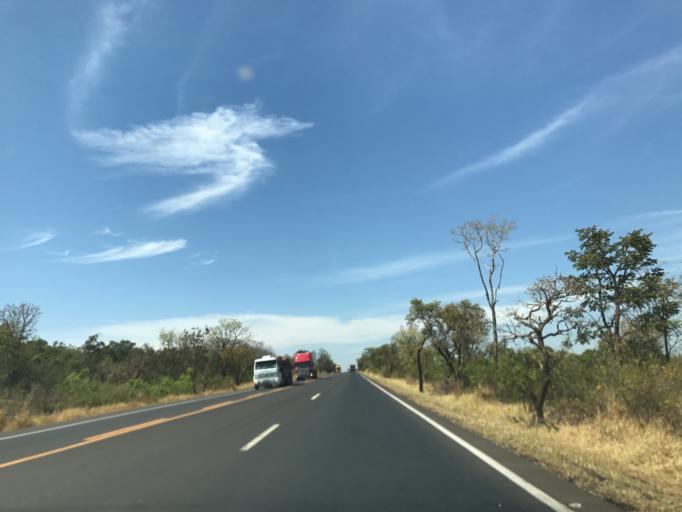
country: BR
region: Minas Gerais
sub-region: Monte Alegre De Minas
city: Monte Alegre de Minas
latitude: -19.0688
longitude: -49.0046
